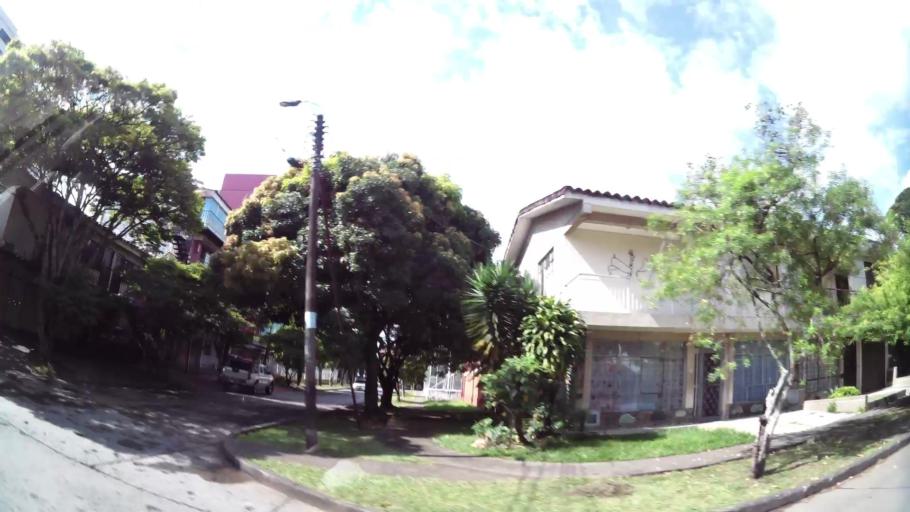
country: CO
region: Valle del Cauca
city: Cali
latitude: 3.4241
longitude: -76.5424
